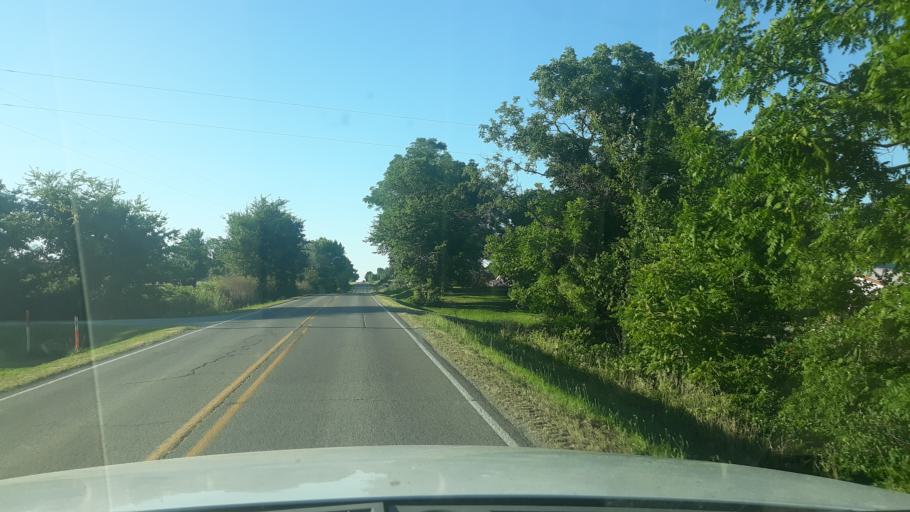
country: US
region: Illinois
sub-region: Saline County
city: Harrisburg
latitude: 37.8519
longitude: -88.6055
